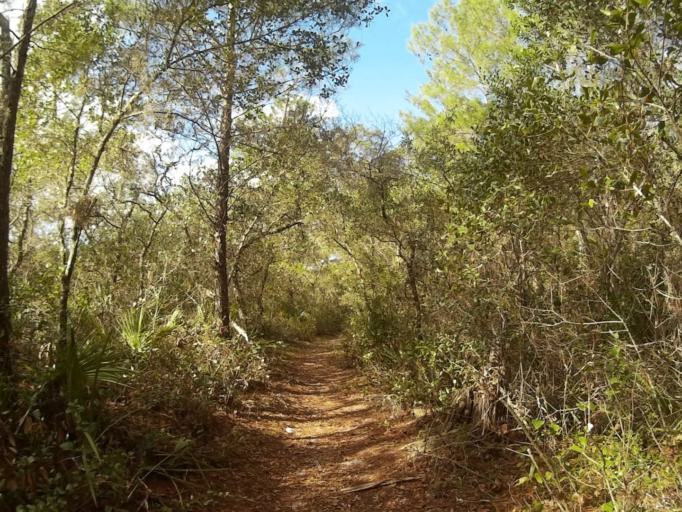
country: US
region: Florida
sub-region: Lake County
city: Astor
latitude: 29.0671
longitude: -81.6095
